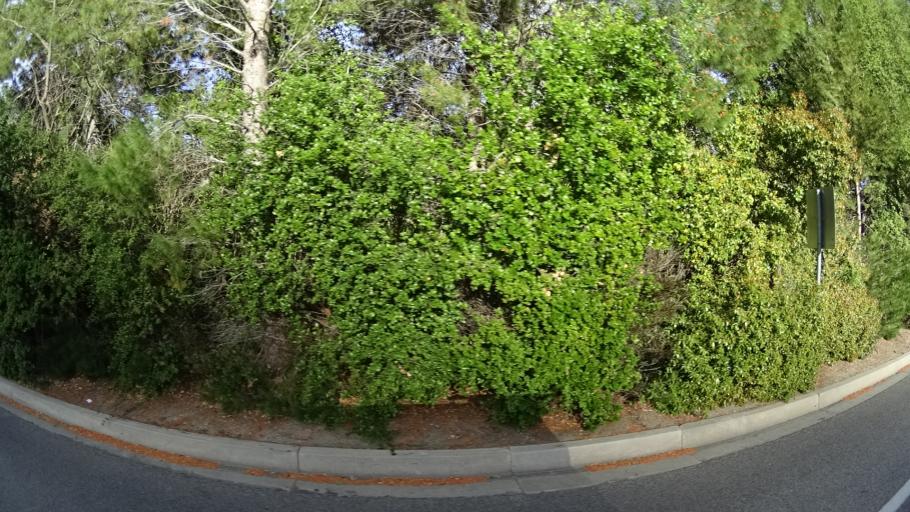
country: US
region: California
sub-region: Ventura County
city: Thousand Oaks
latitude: 34.1756
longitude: -118.8206
